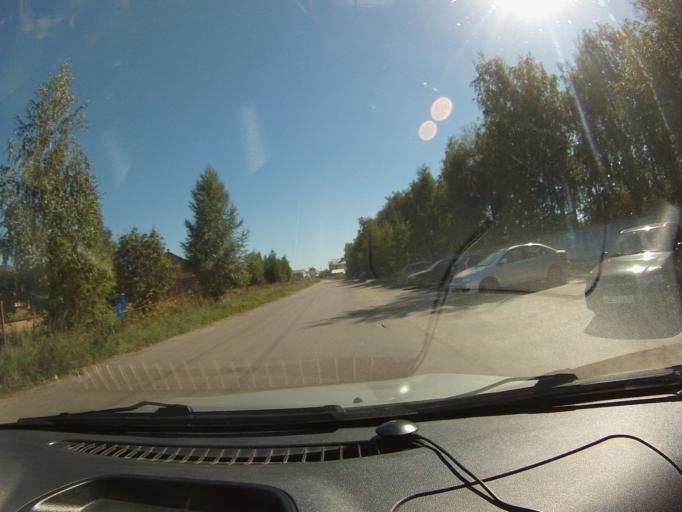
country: RU
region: Tambov
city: Komsomolets
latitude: 52.7675
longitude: 41.3618
